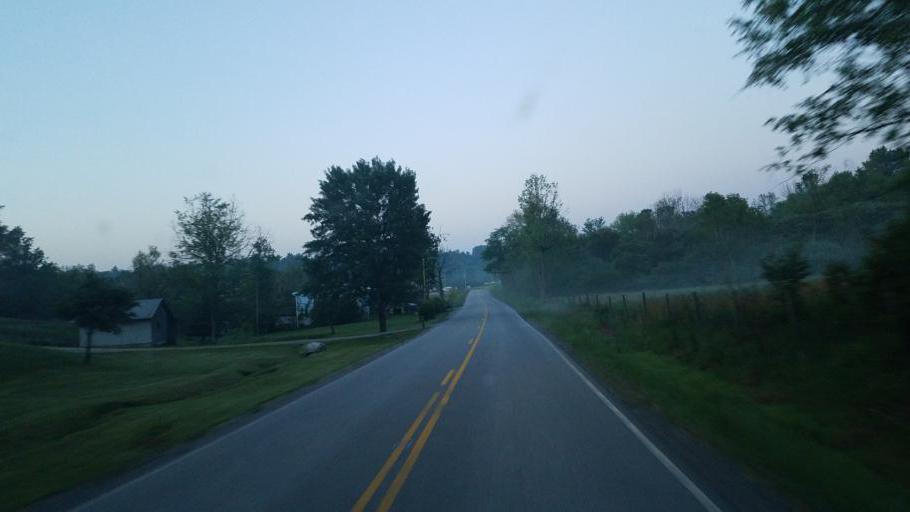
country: US
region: Ohio
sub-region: Belmont County
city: Barnesville
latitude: 40.0582
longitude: -81.3259
